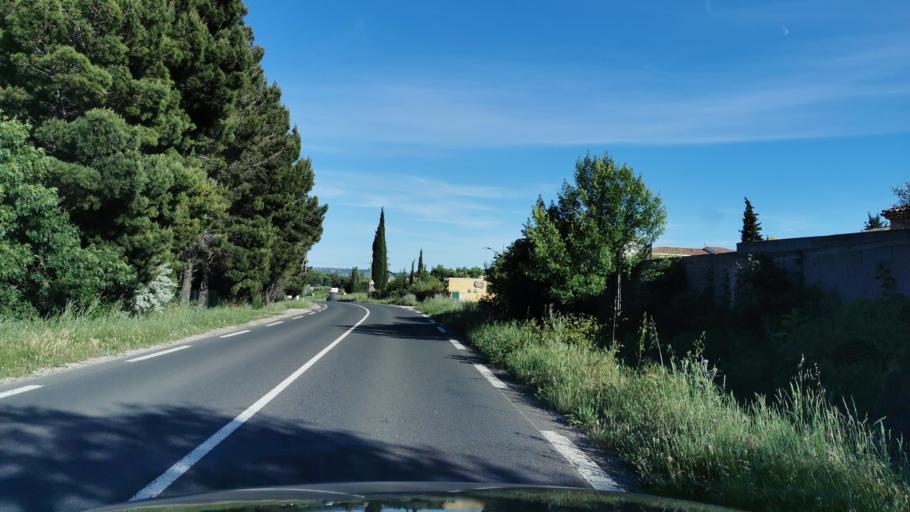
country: FR
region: Languedoc-Roussillon
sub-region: Departement de l'Aude
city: Narbonne
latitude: 43.1996
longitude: 2.9704
